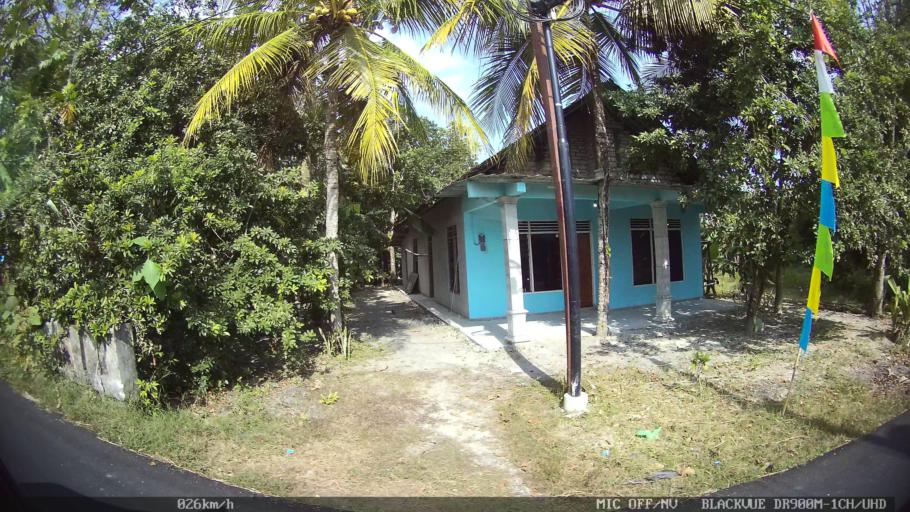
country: ID
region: Daerah Istimewa Yogyakarta
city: Kasihan
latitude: -7.8464
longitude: 110.3013
